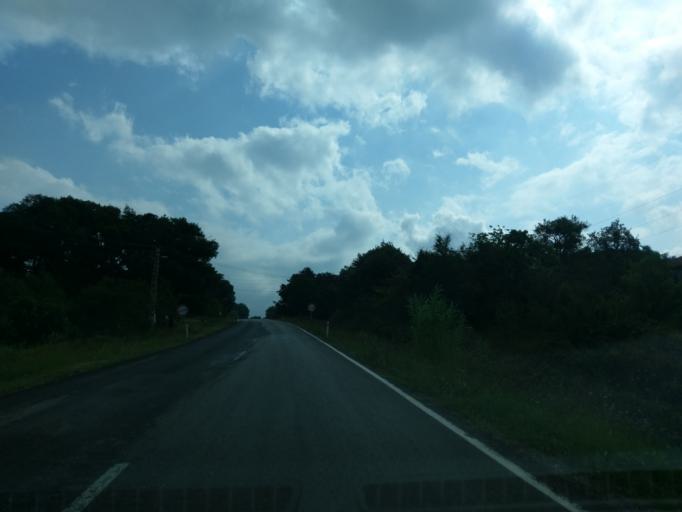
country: TR
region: Sinop
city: Erfelek
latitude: 41.9464
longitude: 34.7907
